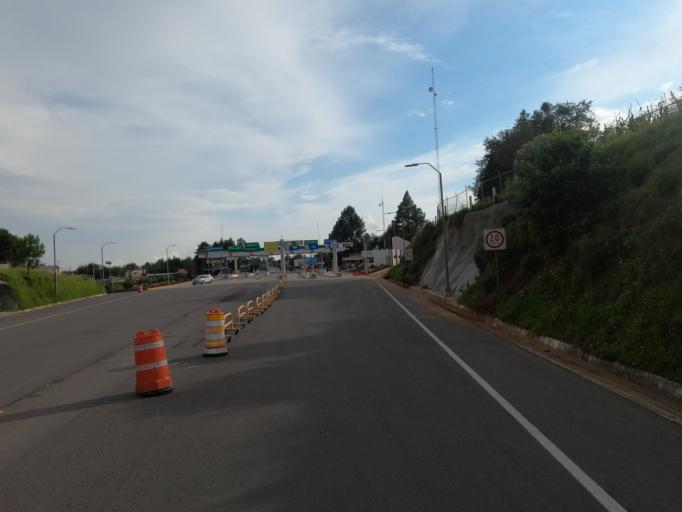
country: MX
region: Mexico
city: Amanalco de Becerra
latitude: 19.3492
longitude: -99.9888
